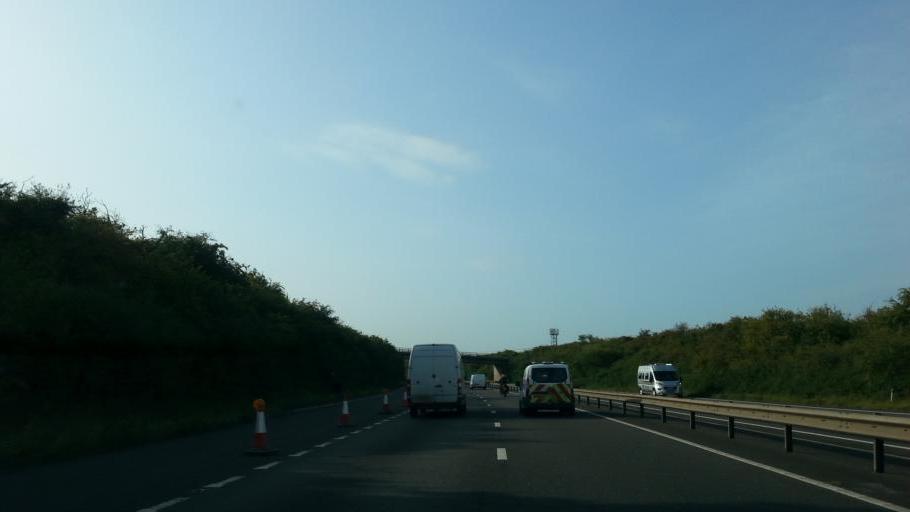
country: GB
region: England
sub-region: Lincolnshire
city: Long Bennington
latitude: 52.9945
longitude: -0.7647
